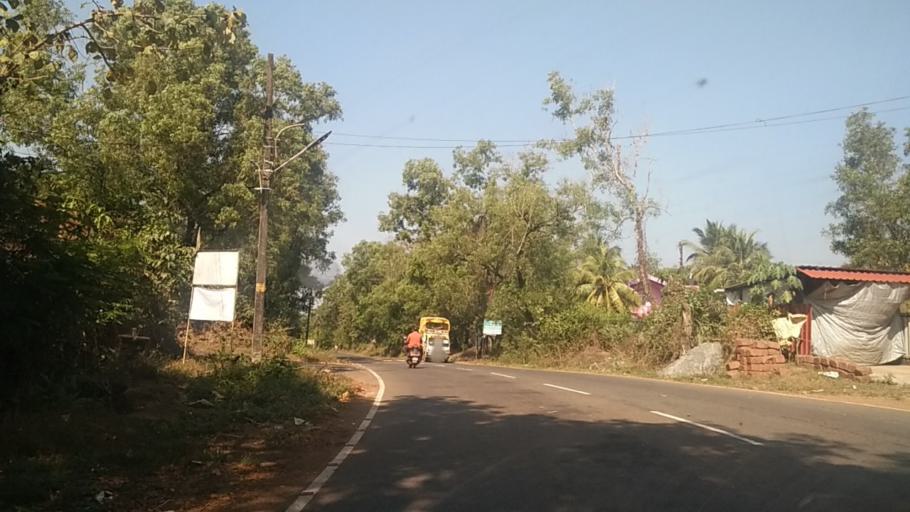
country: IN
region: Goa
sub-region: South Goa
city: Sanguem
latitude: 15.2310
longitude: 74.1321
